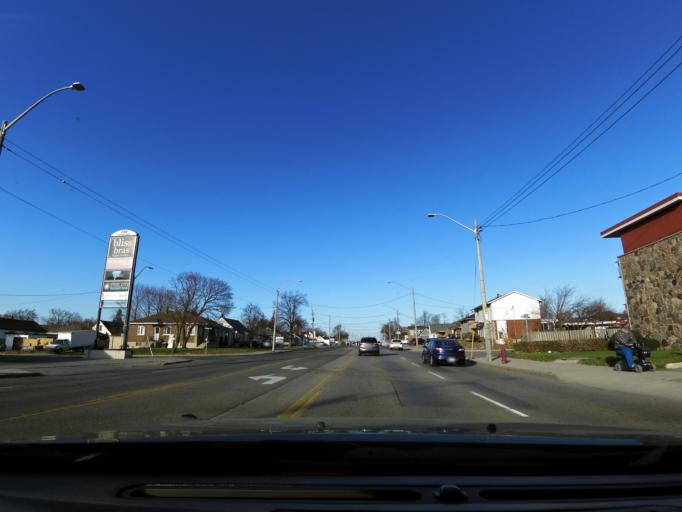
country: CA
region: Ontario
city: Hamilton
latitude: 43.2314
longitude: -79.8805
